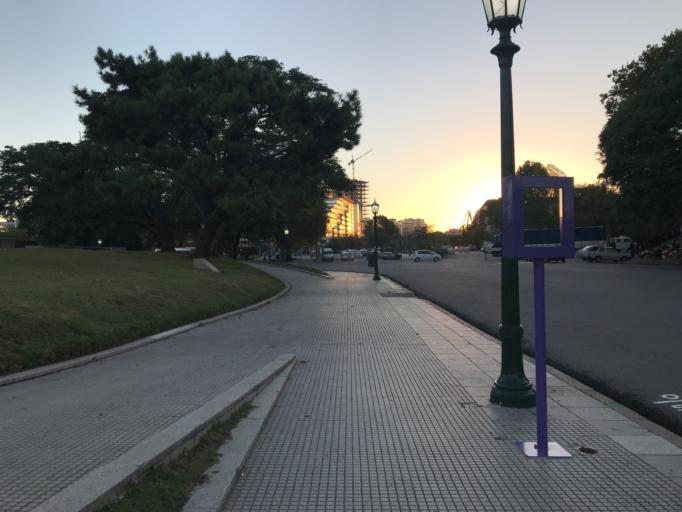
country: AR
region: Buenos Aires F.D.
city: Buenos Aires
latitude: -34.6171
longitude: -58.3572
